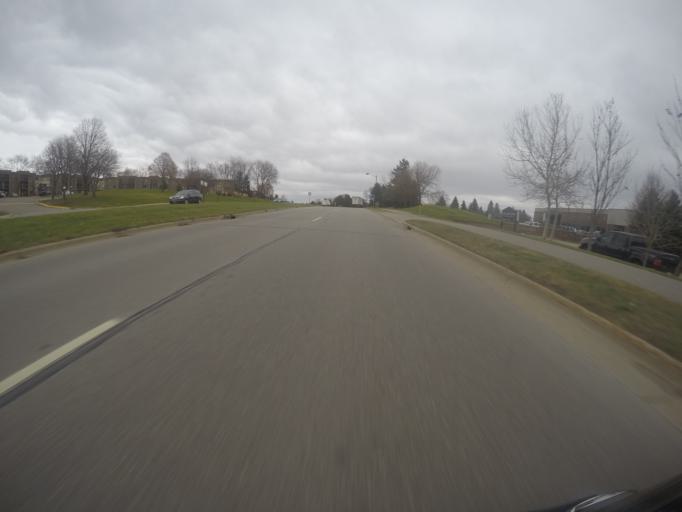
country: US
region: Minnesota
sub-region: Hennepin County
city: Eden Prairie
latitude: 44.8681
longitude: -93.4547
